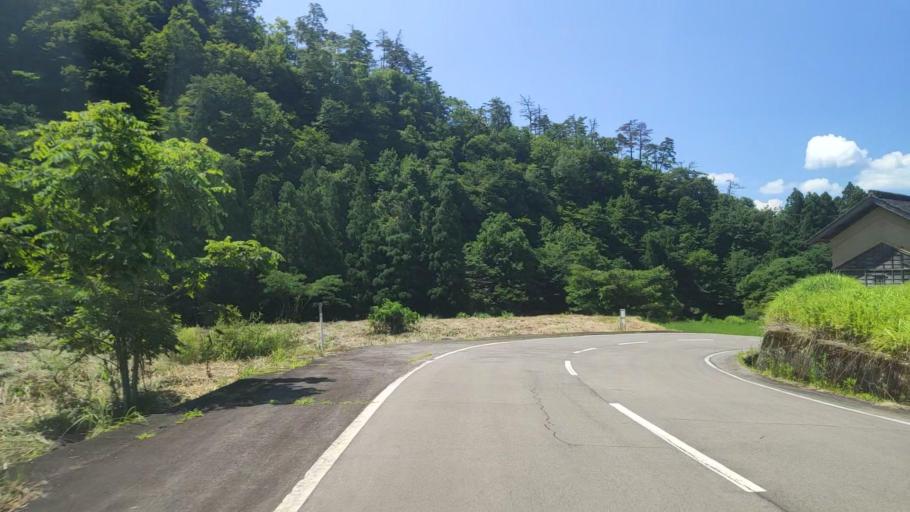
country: JP
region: Fukui
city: Katsuyama
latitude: 36.1123
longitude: 136.5027
